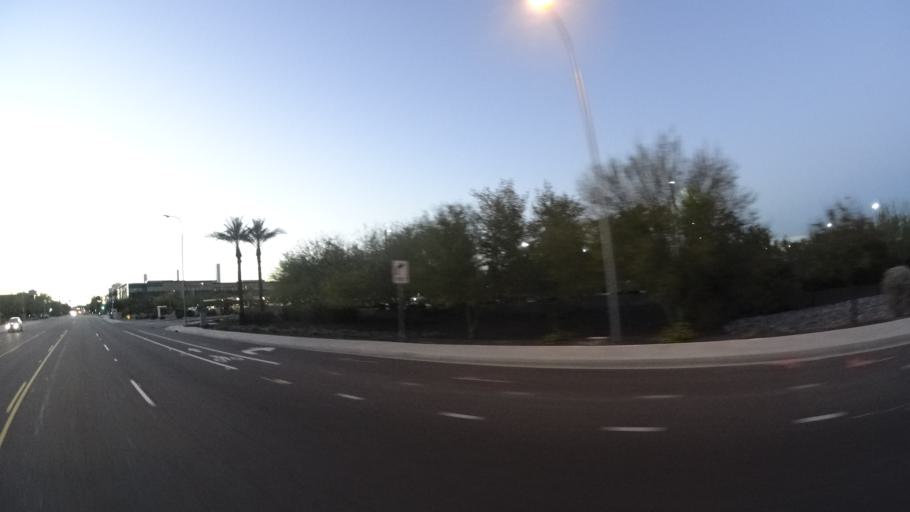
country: US
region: Arizona
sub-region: Maricopa County
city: Chandler
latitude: 33.2987
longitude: -111.8861
